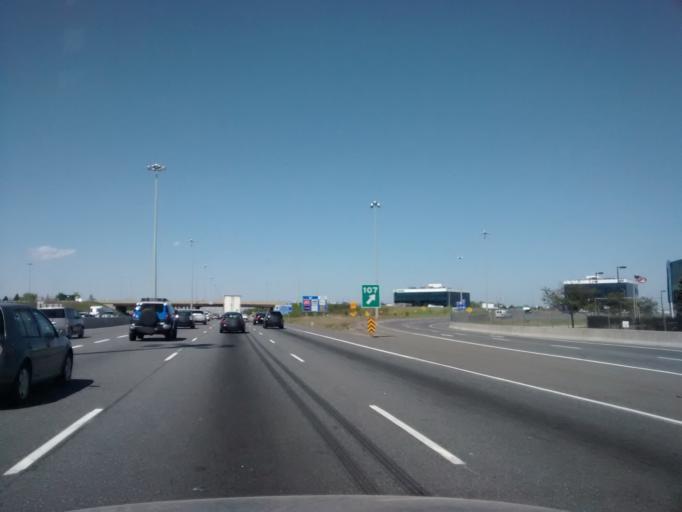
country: CA
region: Ontario
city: Burlington
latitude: 43.3787
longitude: -79.7743
